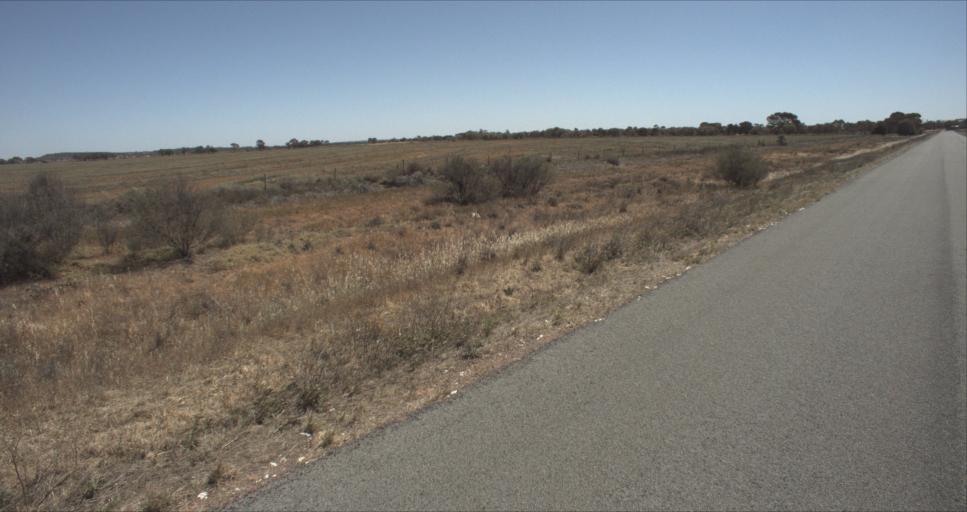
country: AU
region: New South Wales
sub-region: Leeton
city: Leeton
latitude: -34.4345
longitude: 146.2990
